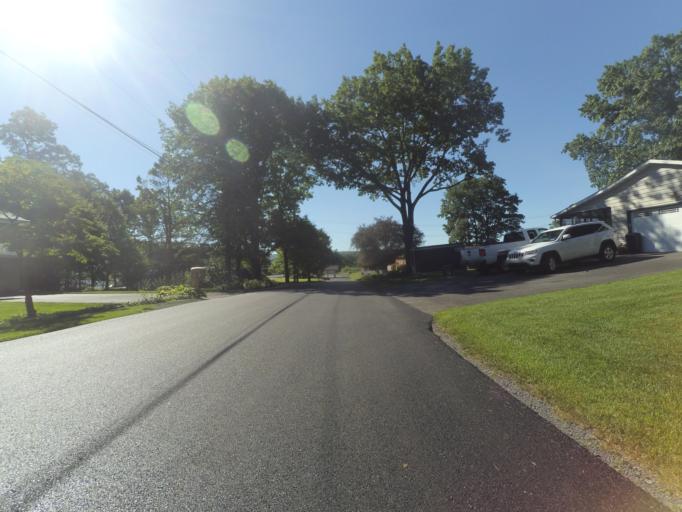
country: US
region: Pennsylvania
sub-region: Centre County
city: Centre Hall
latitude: 40.8347
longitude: -77.6768
